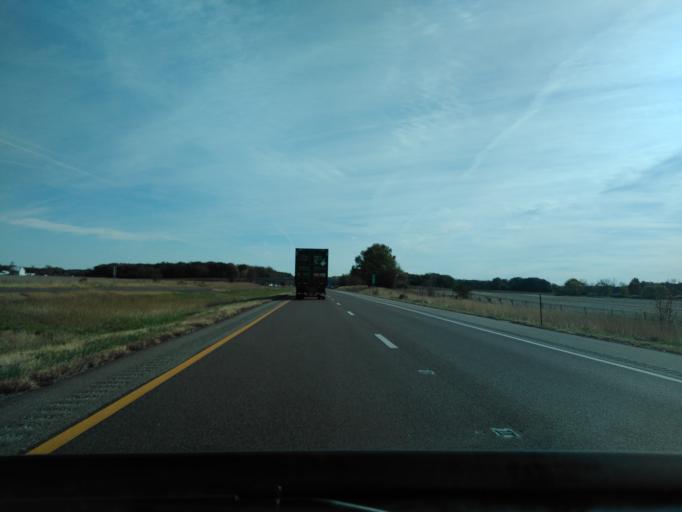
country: US
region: Illinois
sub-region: Madison County
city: Highland
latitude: 38.7854
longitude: -89.7133
